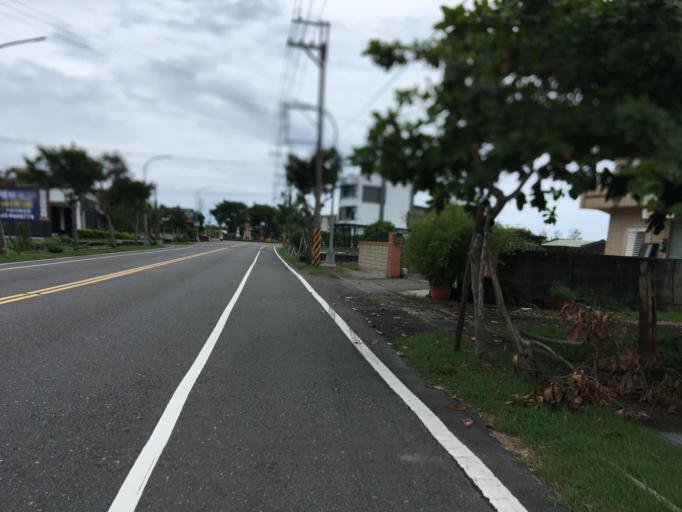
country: TW
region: Taiwan
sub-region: Yilan
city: Yilan
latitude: 24.6924
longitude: 121.8075
